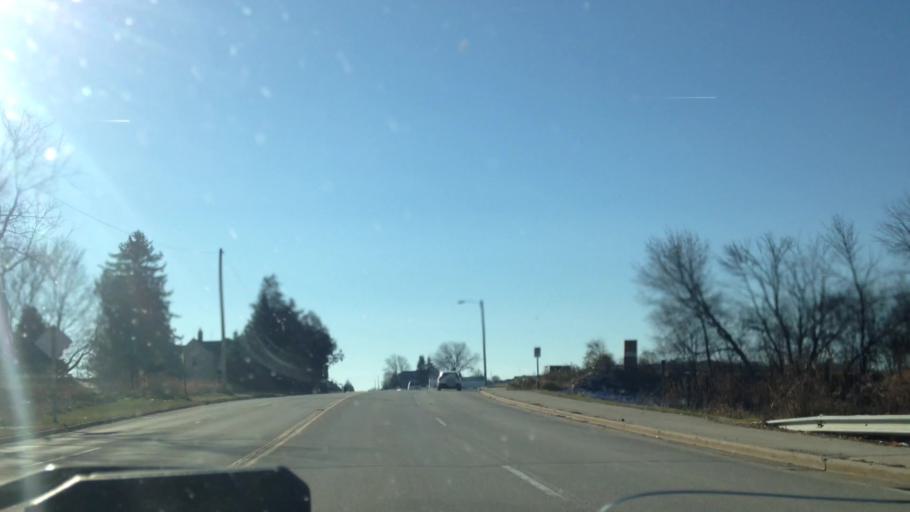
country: US
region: Wisconsin
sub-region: Washington County
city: West Bend
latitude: 43.4257
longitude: -88.1614
